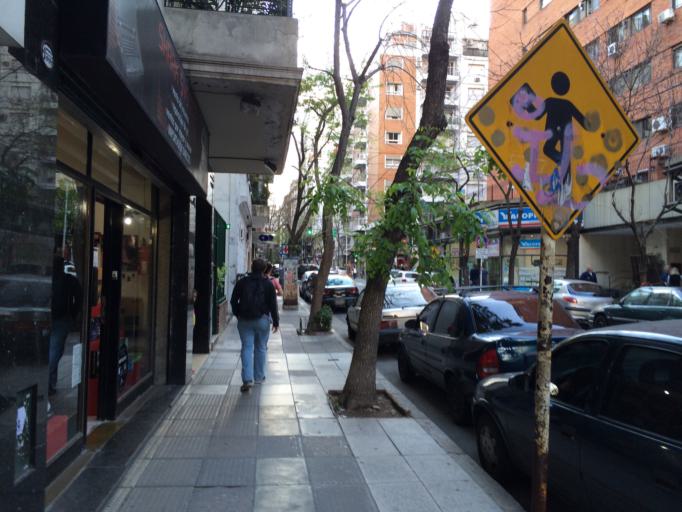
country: AR
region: Buenos Aires F.D.
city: Retiro
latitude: -34.5914
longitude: -58.4046
